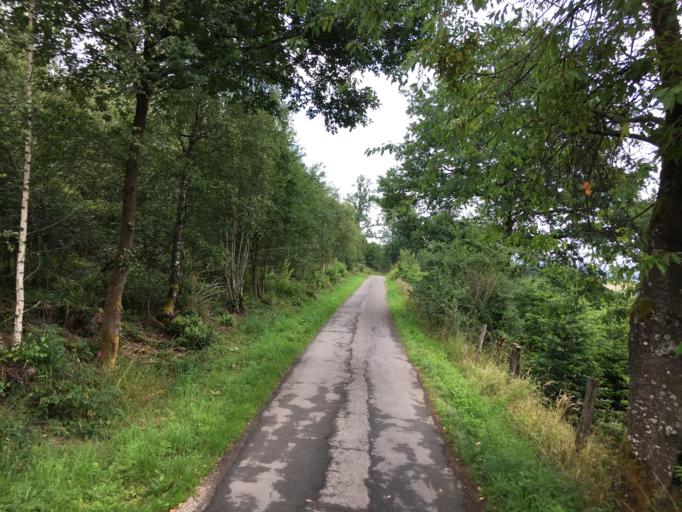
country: DE
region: North Rhine-Westphalia
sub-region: Regierungsbezirk Arnsberg
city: Attendorn
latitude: 51.1148
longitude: 7.8678
